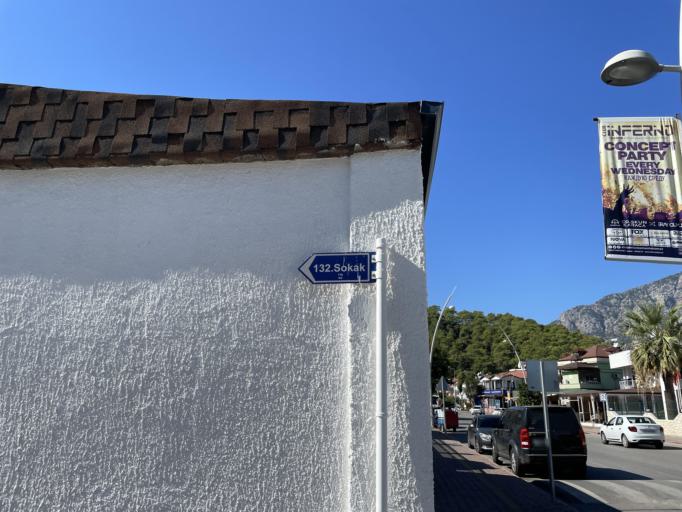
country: TR
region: Antalya
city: Kemer
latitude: 36.5968
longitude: 30.5646
